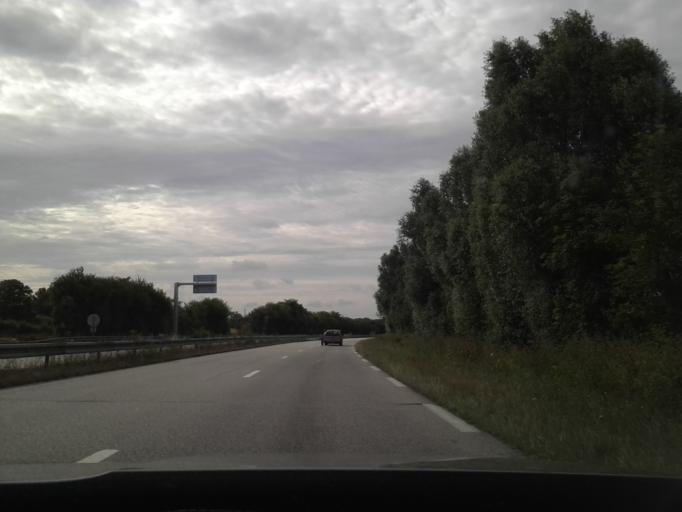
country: FR
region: Lower Normandy
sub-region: Departement de la Manche
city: Montebourg
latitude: 49.4745
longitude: -1.3691
